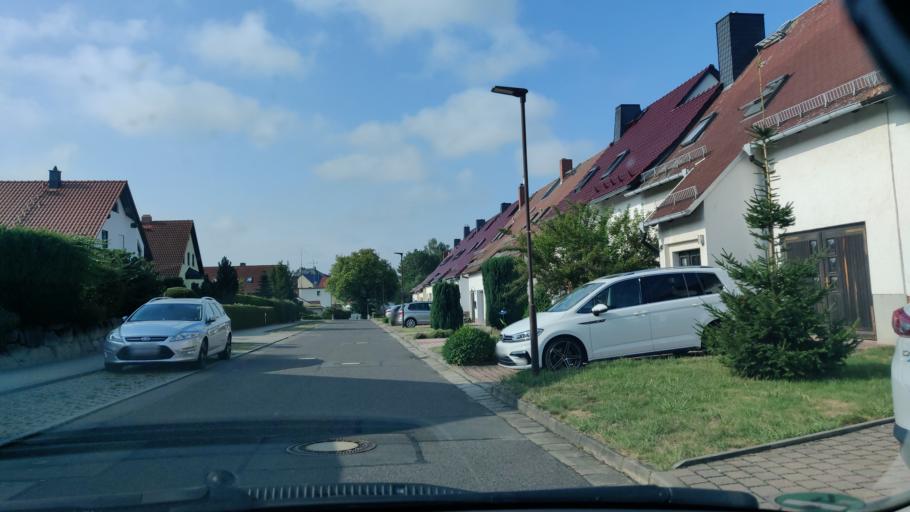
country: DE
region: Saxony
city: Geithain
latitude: 51.0546
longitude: 12.7028
